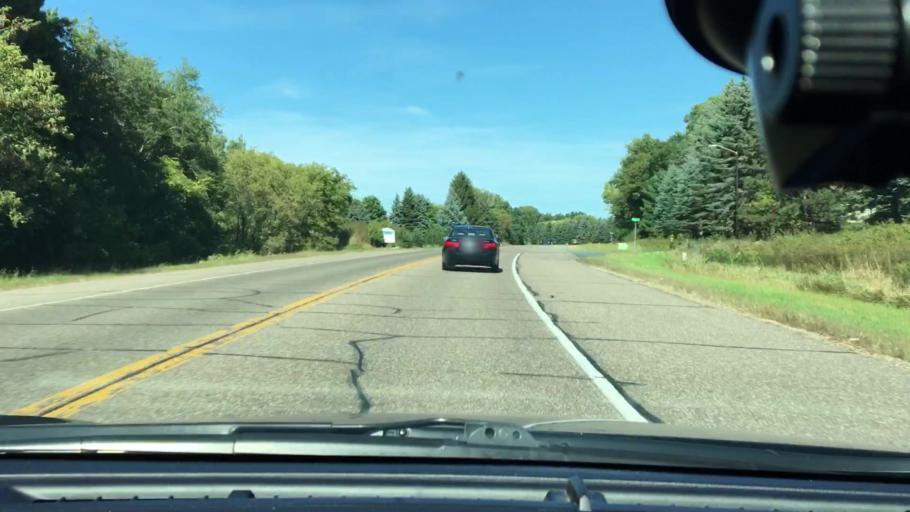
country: US
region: Minnesota
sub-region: Washington County
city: Mahtomedi
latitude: 45.0469
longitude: -92.9498
